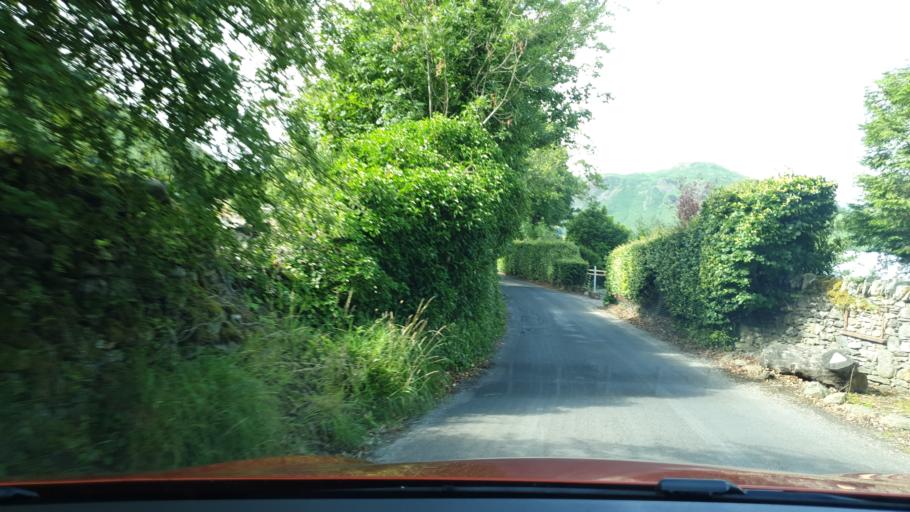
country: GB
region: England
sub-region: Cumbria
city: Penrith
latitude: 54.5817
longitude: -2.8521
